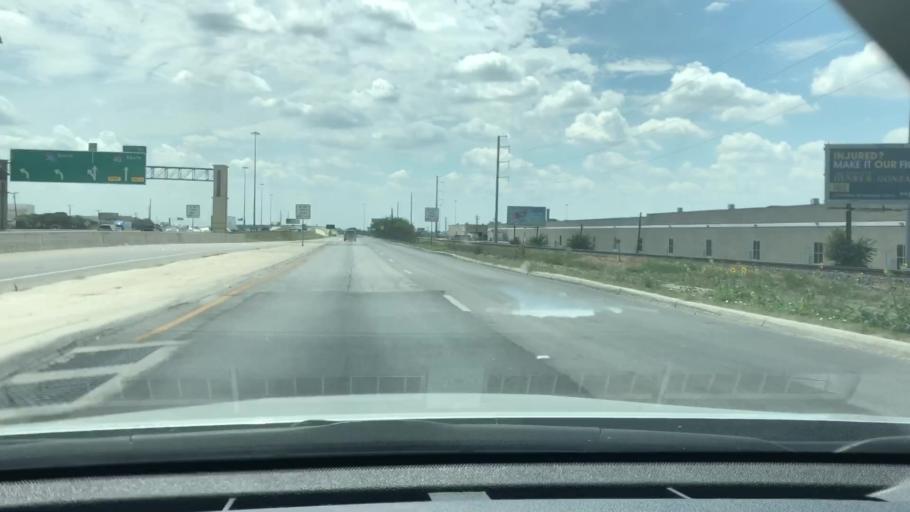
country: US
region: Texas
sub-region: Bexar County
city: Kirby
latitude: 29.4811
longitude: -98.4042
